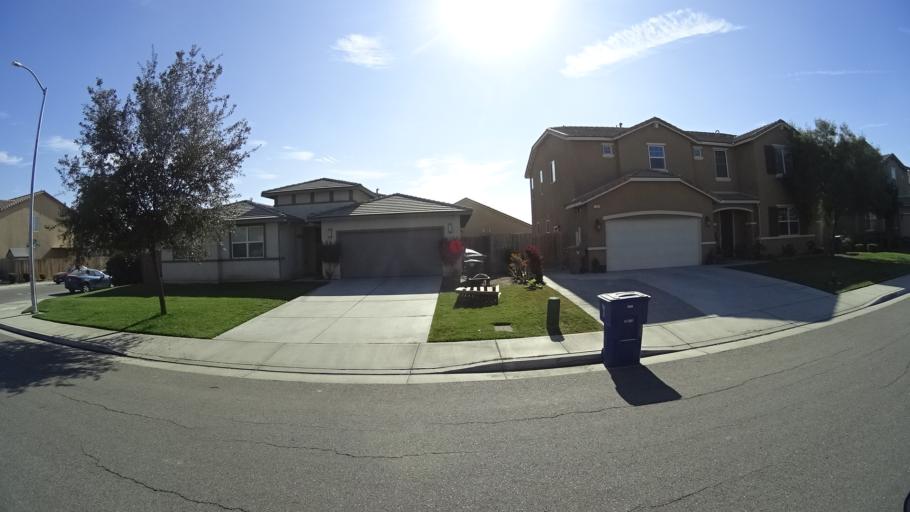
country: US
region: California
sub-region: Kern County
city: Greenfield
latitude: 35.2859
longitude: -119.0603
